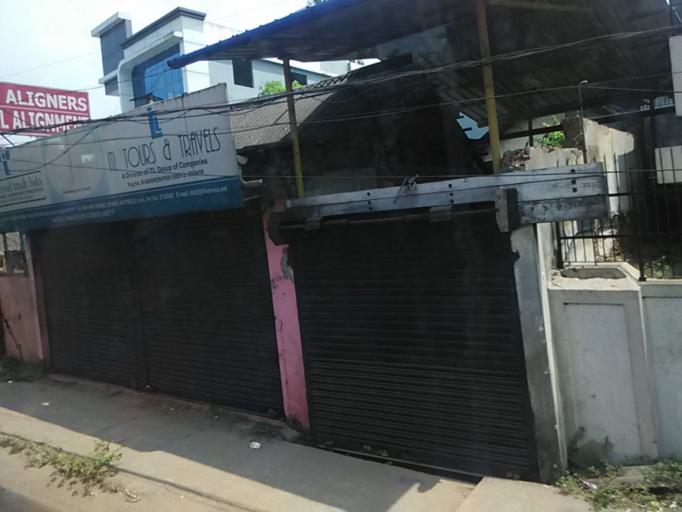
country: IN
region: Kerala
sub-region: Kozhikode
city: Kozhikode
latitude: 11.2650
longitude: 75.7772
